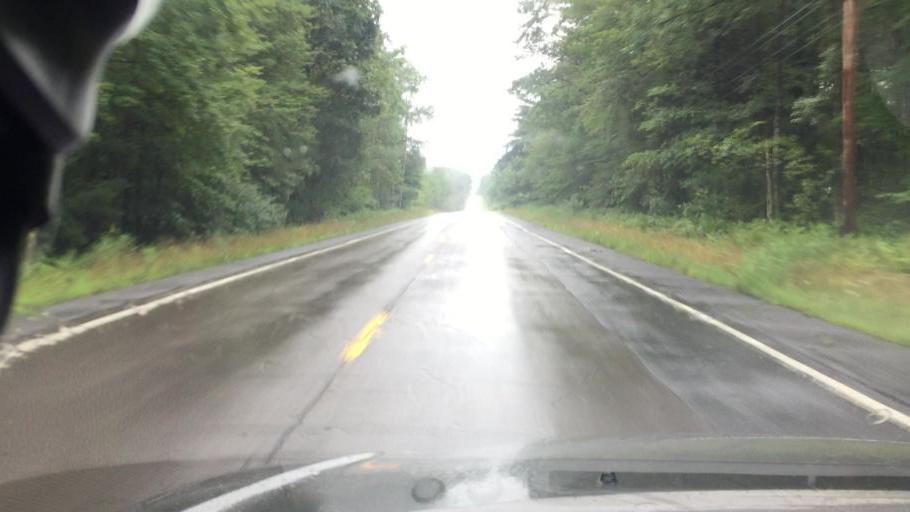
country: US
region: Pennsylvania
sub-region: Luzerne County
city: Freeland
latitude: 41.0323
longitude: -75.8520
